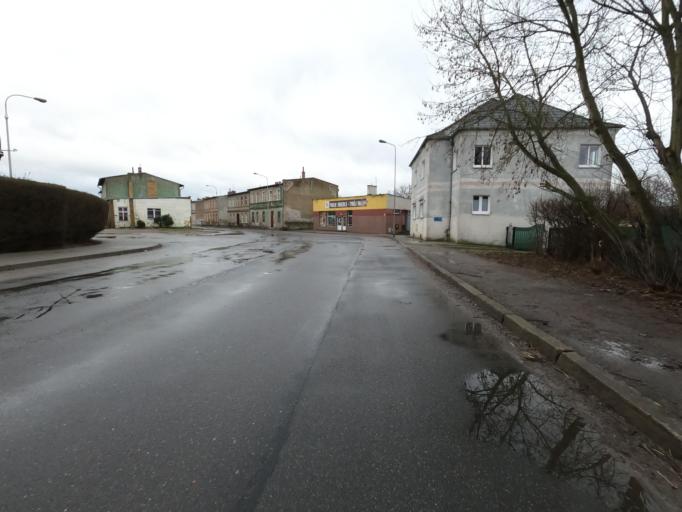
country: PL
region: Greater Poland Voivodeship
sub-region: Powiat pilski
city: Pila
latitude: 53.1437
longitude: 16.7558
